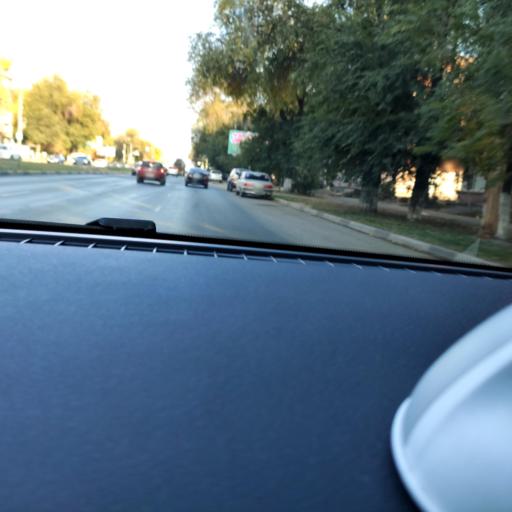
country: RU
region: Samara
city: Samara
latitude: 53.2005
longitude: 50.1871
